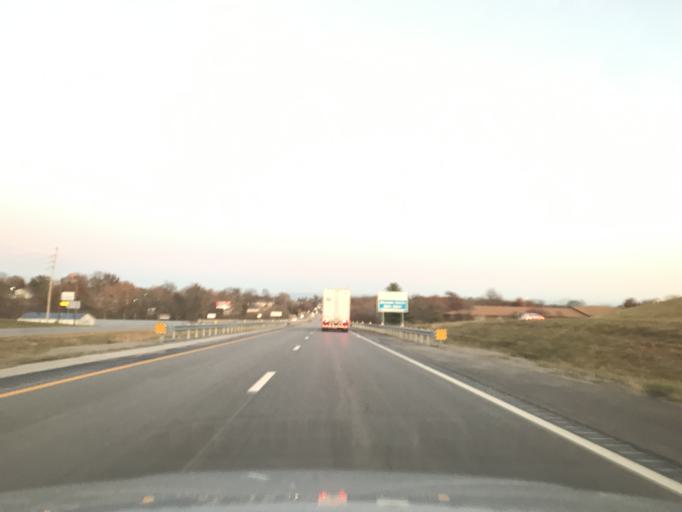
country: US
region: Missouri
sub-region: Marion County
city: Hannibal
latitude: 39.7144
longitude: -91.4023
